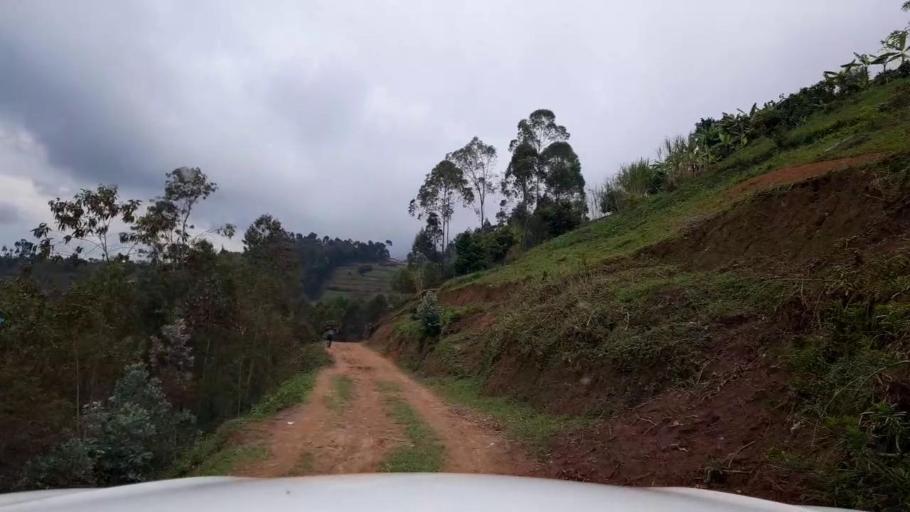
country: RW
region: Northern Province
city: Musanze
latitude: -1.5967
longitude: 29.7796
